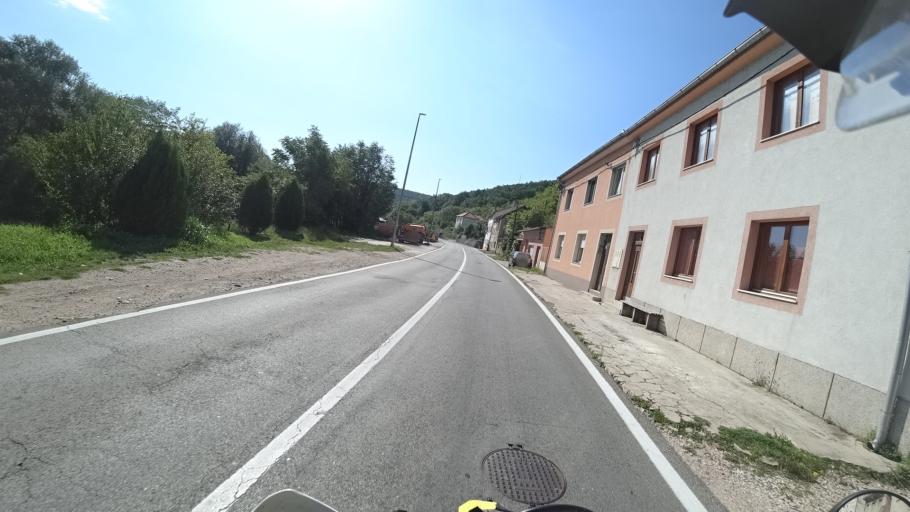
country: HR
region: Sibensko-Kniniska
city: Knin
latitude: 44.0315
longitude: 16.1898
